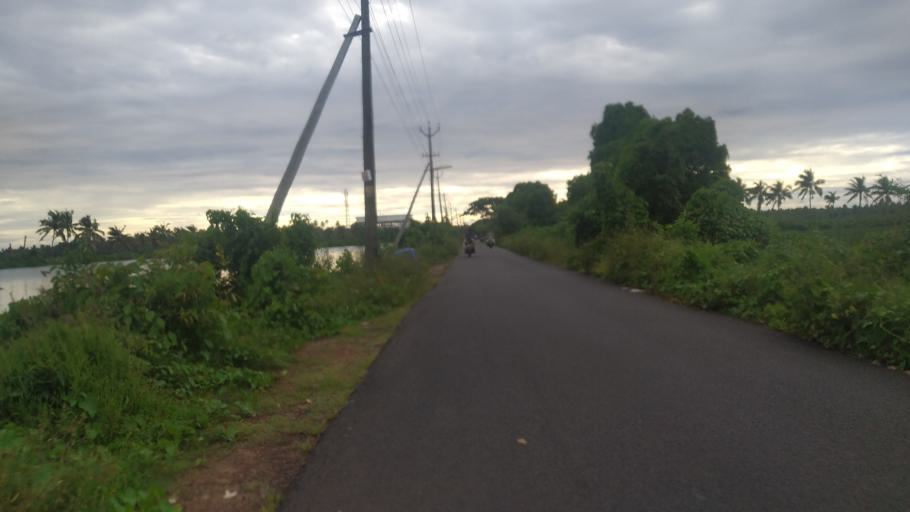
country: IN
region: Kerala
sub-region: Alappuzha
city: Arukutti
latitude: 9.8577
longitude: 76.2754
